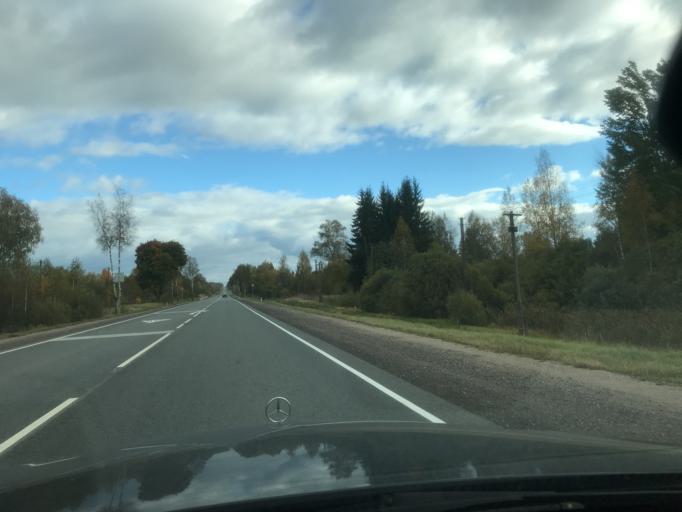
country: RU
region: Pskov
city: Opochka
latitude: 56.6718
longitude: 28.7265
